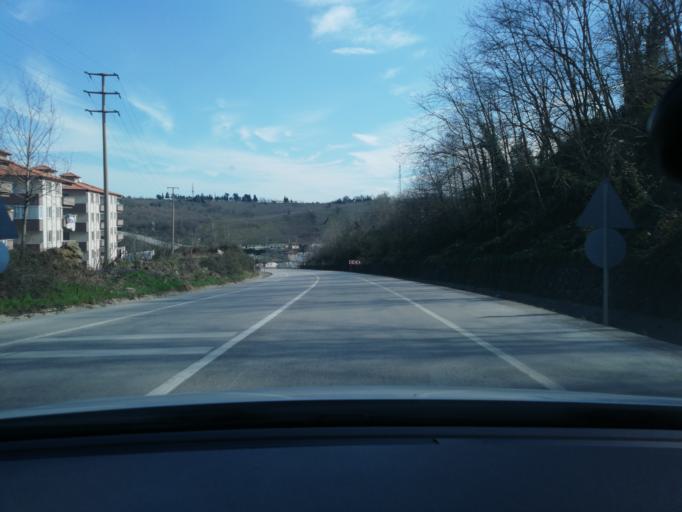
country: TR
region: Duzce
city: Akcakoca
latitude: 41.0773
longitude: 31.1242
